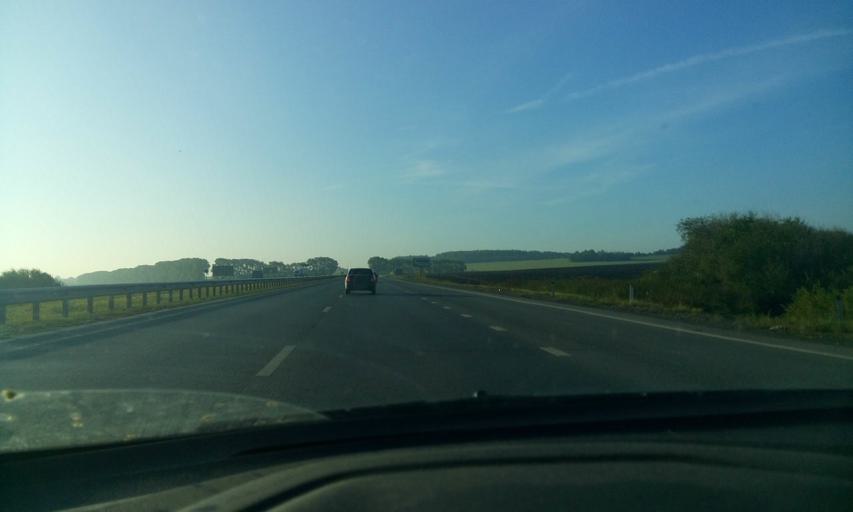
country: RU
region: Sverdlovsk
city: Aramil
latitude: 56.6767
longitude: 60.7809
